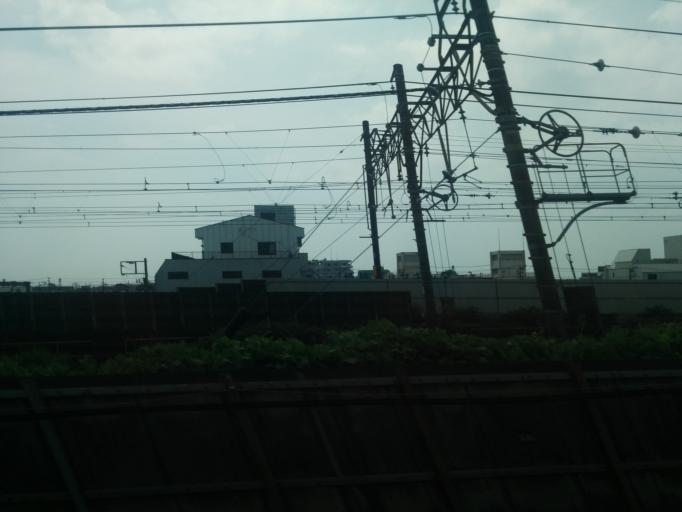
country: JP
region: Kanagawa
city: Odawara
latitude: 35.2633
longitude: 139.1617
